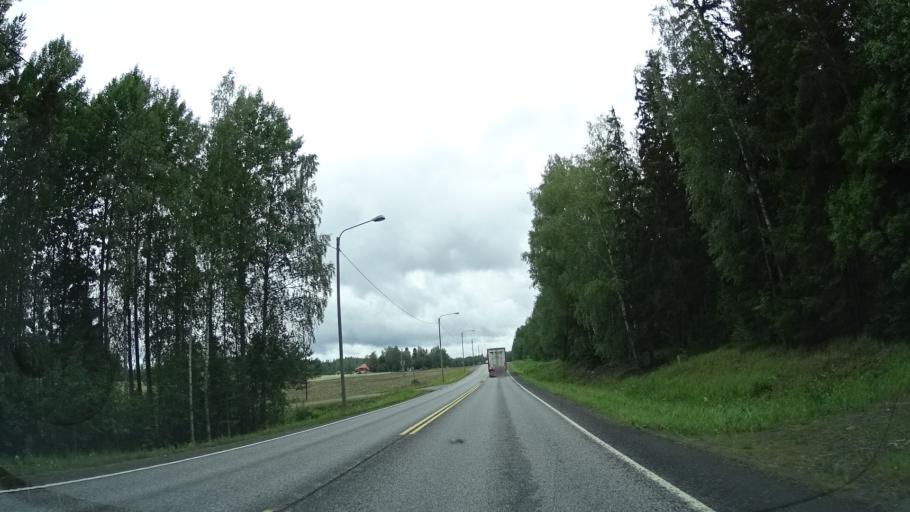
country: FI
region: Uusimaa
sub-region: Helsinki
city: Karkkila
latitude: 60.4926
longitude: 24.2812
